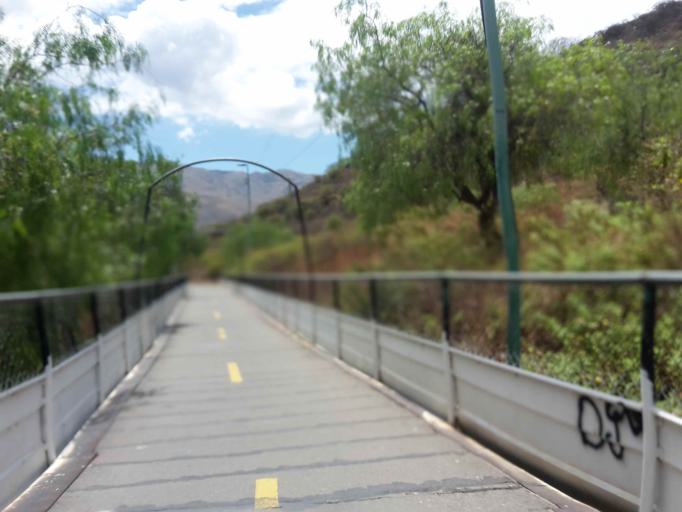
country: BO
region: Cochabamba
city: Cochabamba
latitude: -17.3819
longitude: -66.1417
